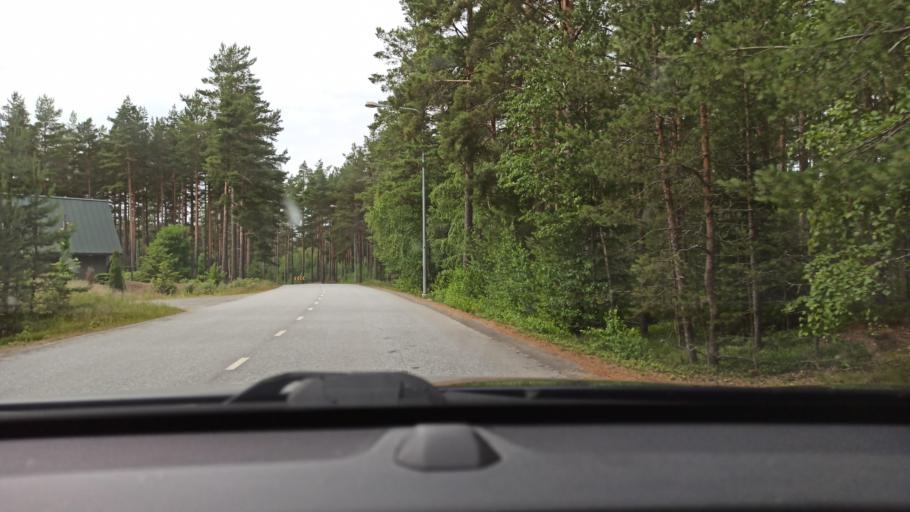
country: FI
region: Satakunta
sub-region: Pori
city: Luvia
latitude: 61.5746
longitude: 21.5261
